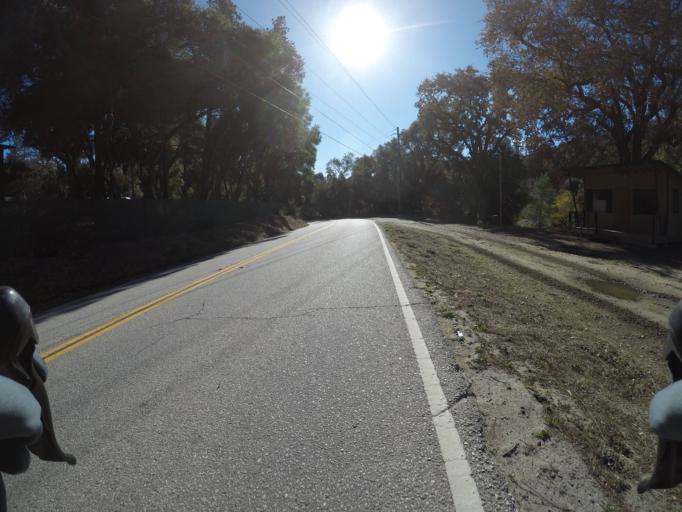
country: US
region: California
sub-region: Santa Cruz County
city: Mount Hermon
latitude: 37.0670
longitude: -122.0575
